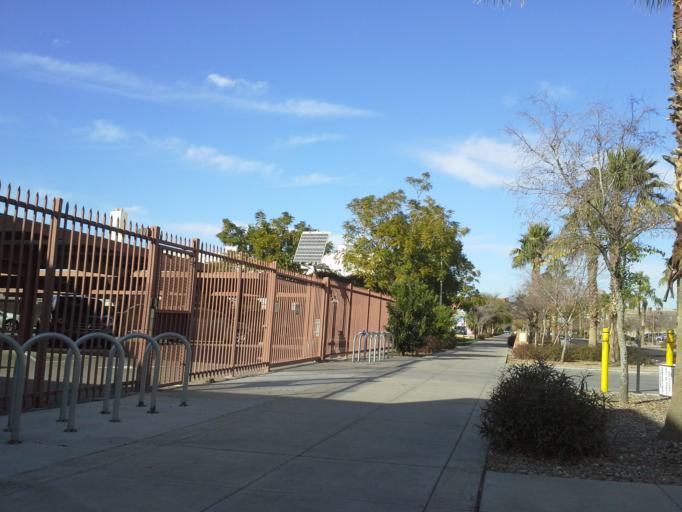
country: US
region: Arizona
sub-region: Maricopa County
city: Phoenix
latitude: 33.4518
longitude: -112.0765
